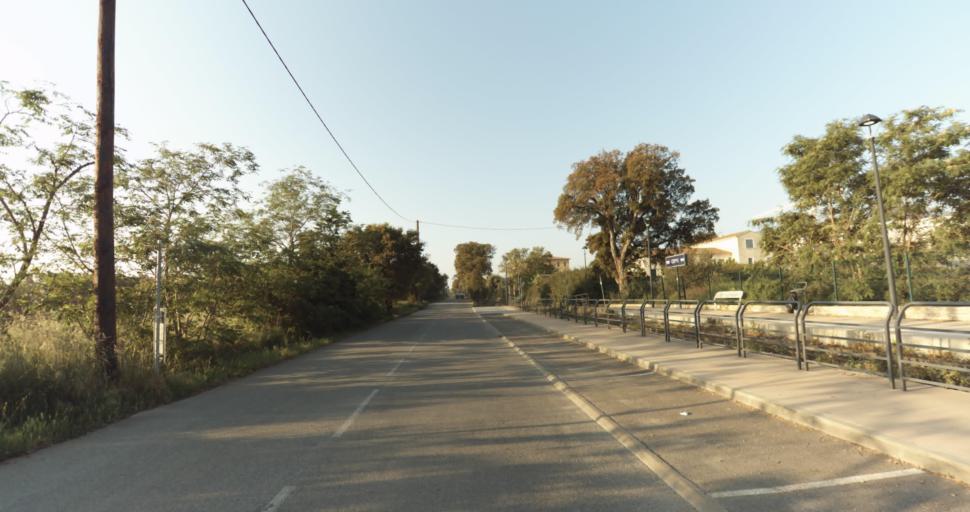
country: FR
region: Corsica
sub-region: Departement de la Haute-Corse
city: Biguglia
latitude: 42.6285
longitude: 9.4409
